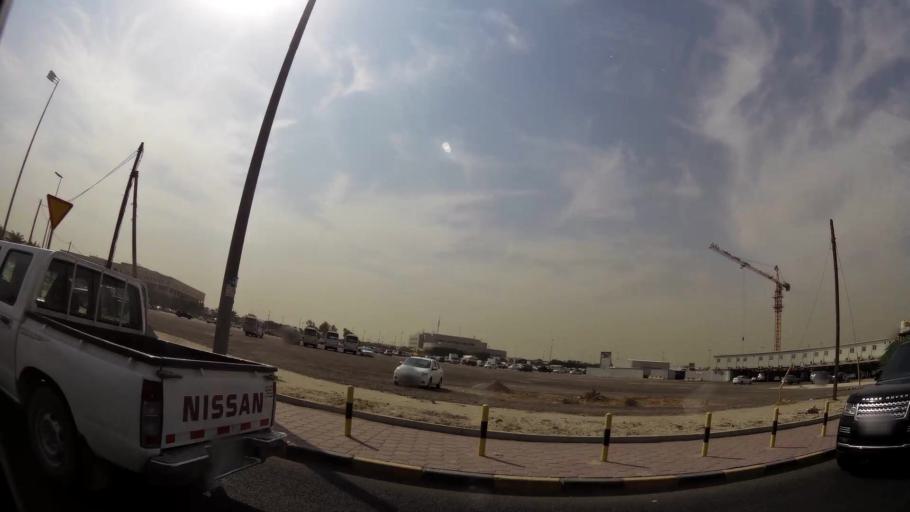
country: KW
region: Al Farwaniyah
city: Janub as Surrah
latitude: 29.2713
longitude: 48.0154
